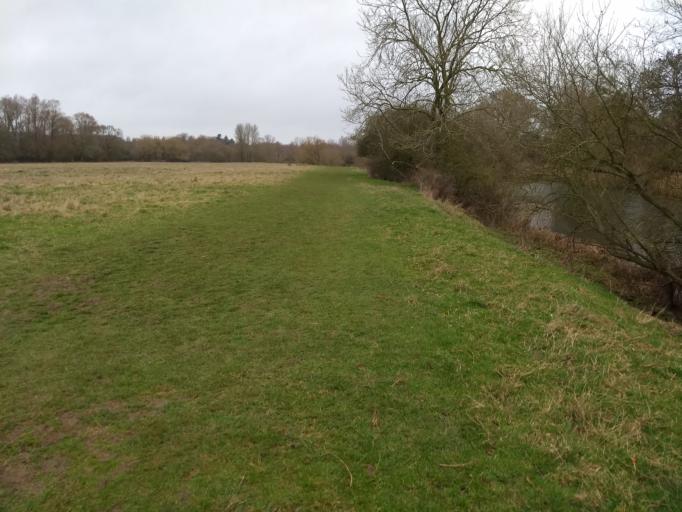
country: GB
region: England
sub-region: Bedford
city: Odell
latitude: 52.2026
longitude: -0.5908
